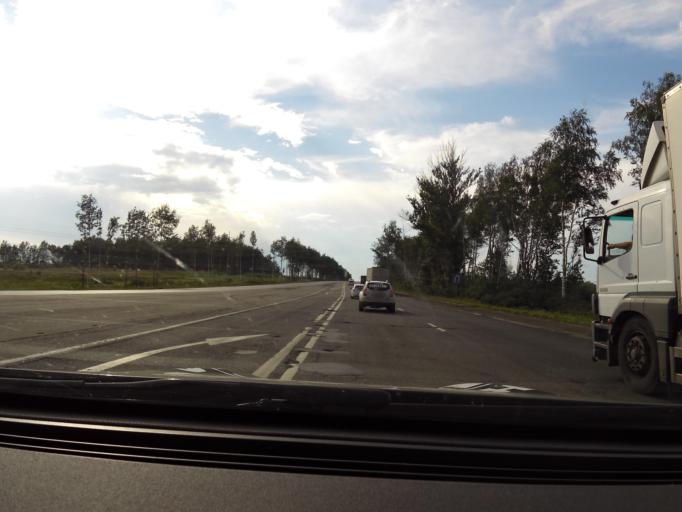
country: RU
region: Vladimir
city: Novovyazniki
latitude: 56.1941
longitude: 42.3781
